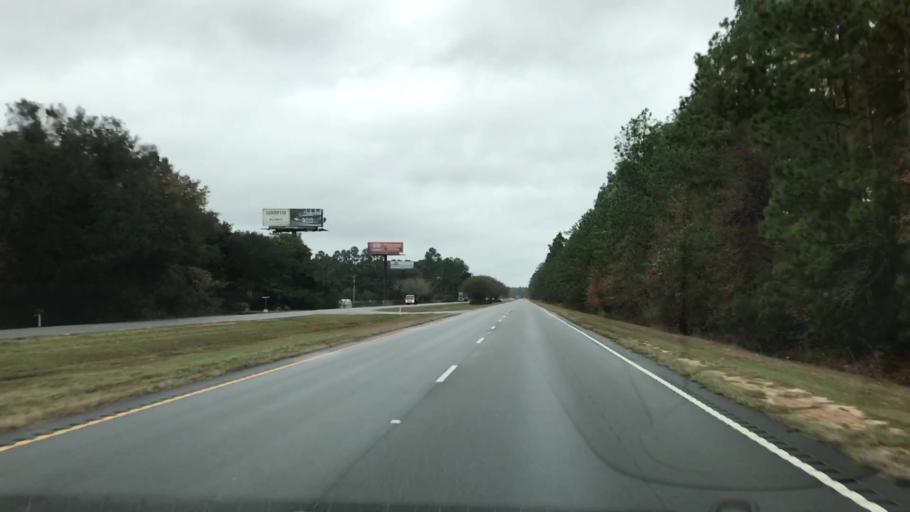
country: US
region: South Carolina
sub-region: Georgetown County
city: Georgetown
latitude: 33.2339
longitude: -79.3759
